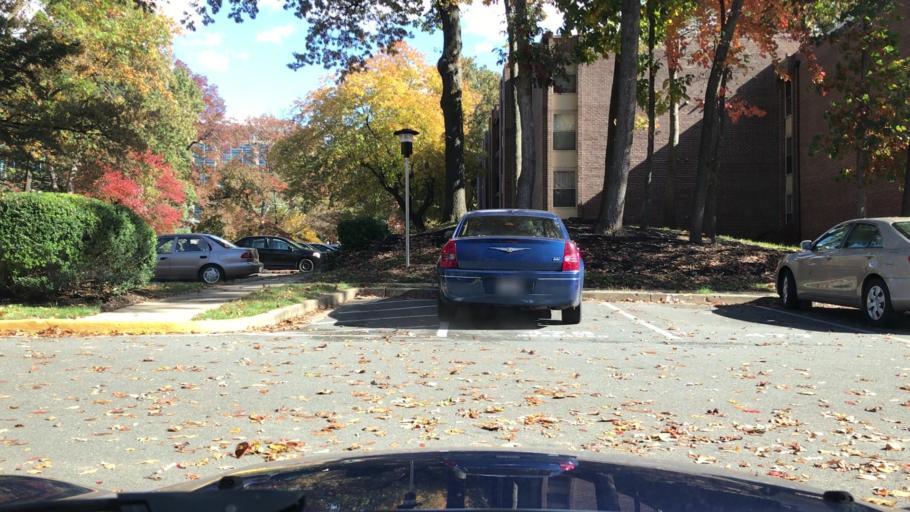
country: US
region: Virginia
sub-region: Fairfax County
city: Merrifield
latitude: 38.8563
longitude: -77.2314
